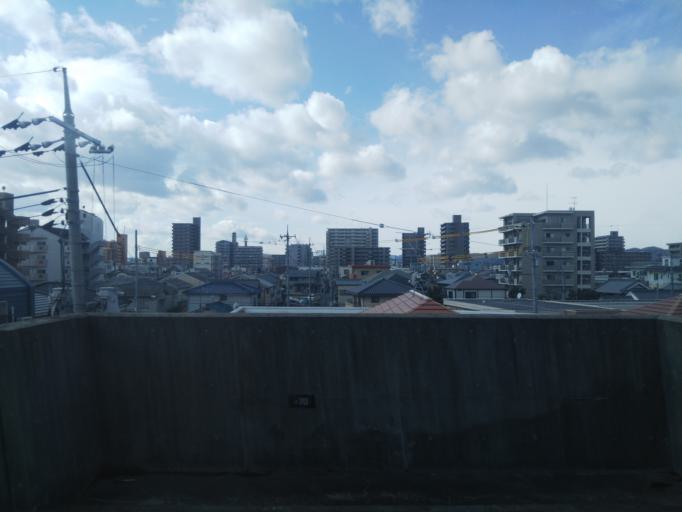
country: JP
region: Okayama
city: Okayama-shi
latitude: 34.6478
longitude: 133.9108
